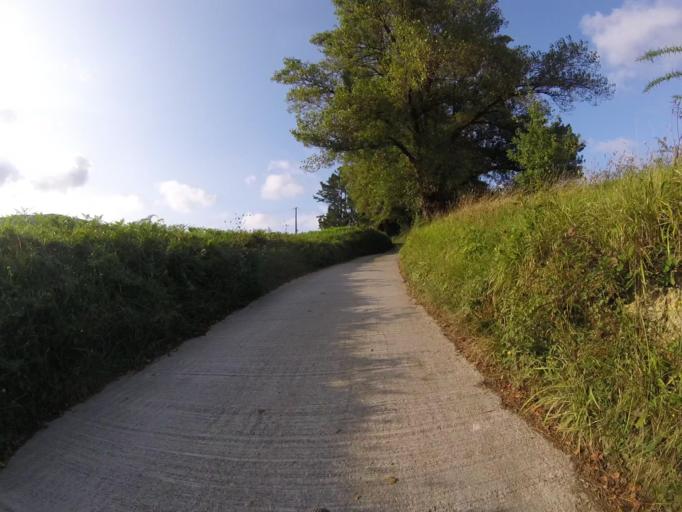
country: ES
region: Basque Country
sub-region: Provincia de Guipuzcoa
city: Fuenterrabia
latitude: 43.3557
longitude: -1.8122
